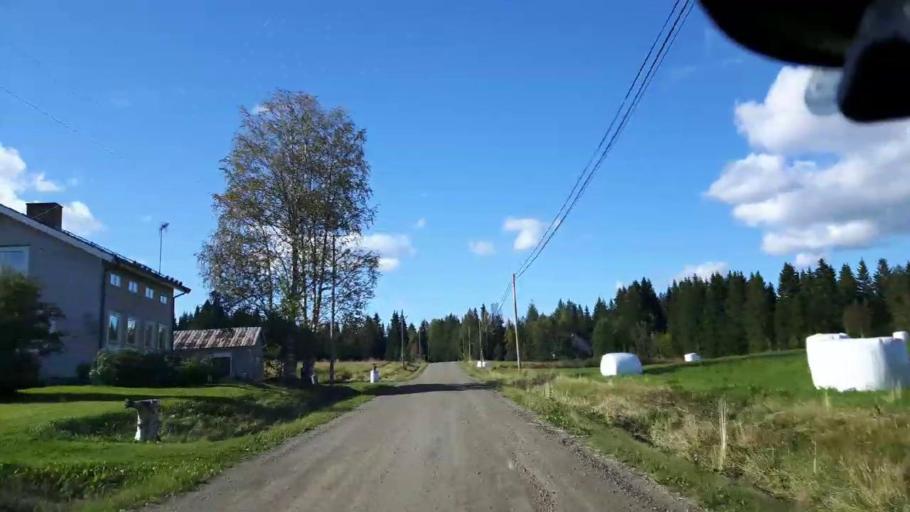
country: SE
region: Vaesternorrland
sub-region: Solleftea Kommun
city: As
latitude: 63.4598
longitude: 16.2562
